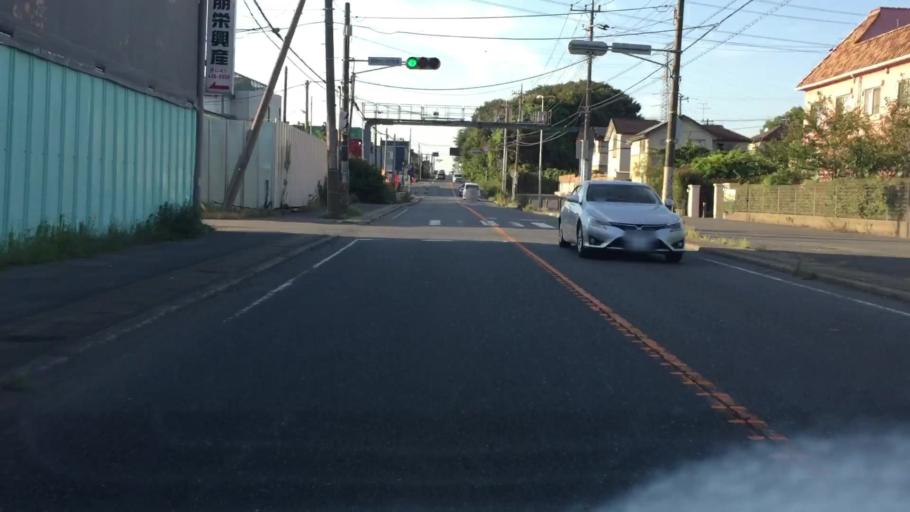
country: JP
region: Chiba
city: Funabashi
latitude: 35.7335
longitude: 140.0016
